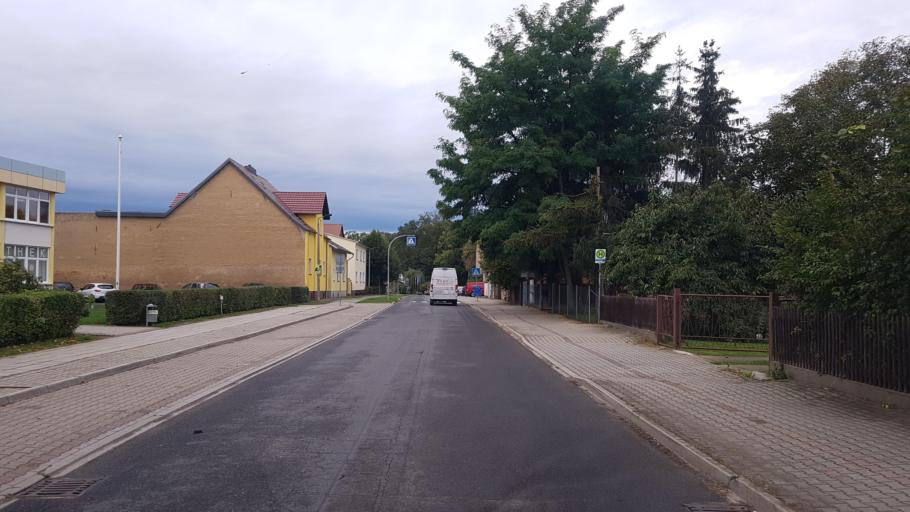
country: DE
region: Brandenburg
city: Golssen
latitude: 51.9715
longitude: 13.6006
